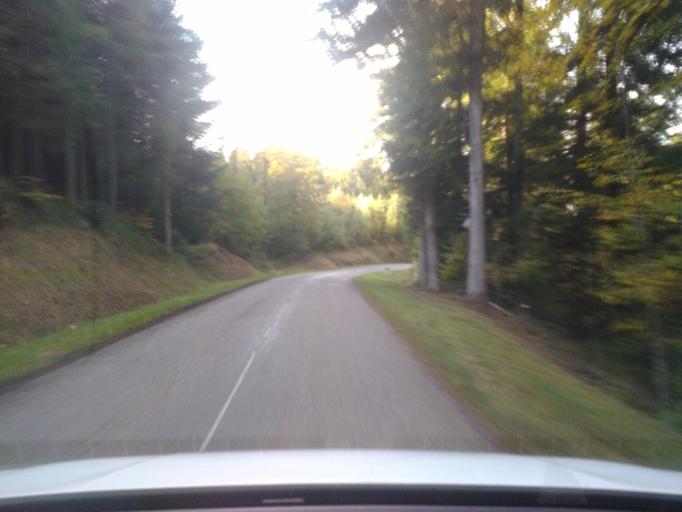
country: FR
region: Lorraine
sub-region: Departement des Vosges
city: Sainte-Marguerite
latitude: 48.3206
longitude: 7.0334
